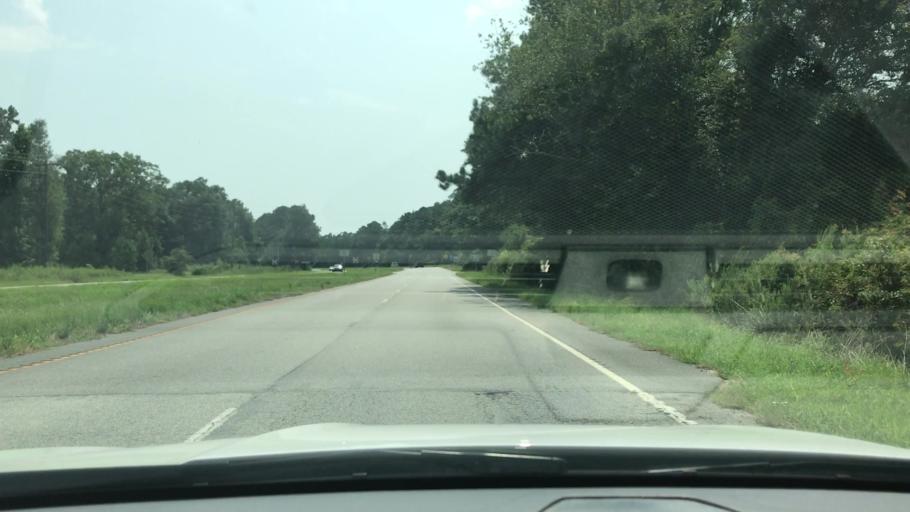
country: US
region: South Carolina
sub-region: Charleston County
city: Awendaw
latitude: 32.9399
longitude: -79.7094
